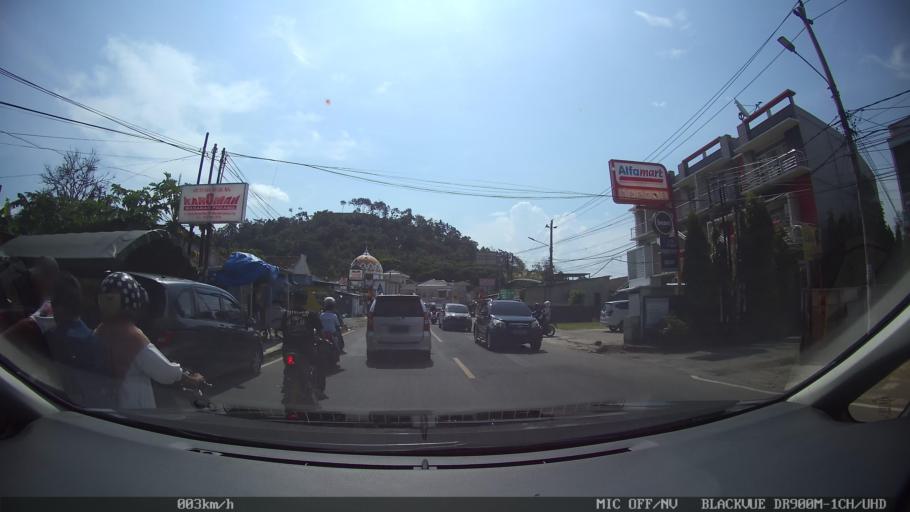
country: ID
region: Lampung
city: Kedaton
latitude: -5.3996
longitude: 105.2446
